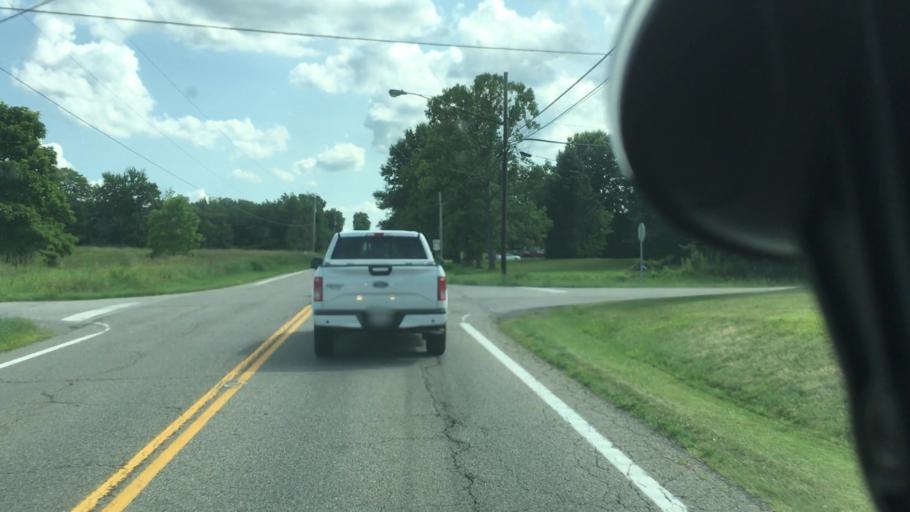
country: US
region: Ohio
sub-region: Columbiana County
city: Salem
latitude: 40.9732
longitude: -80.8281
